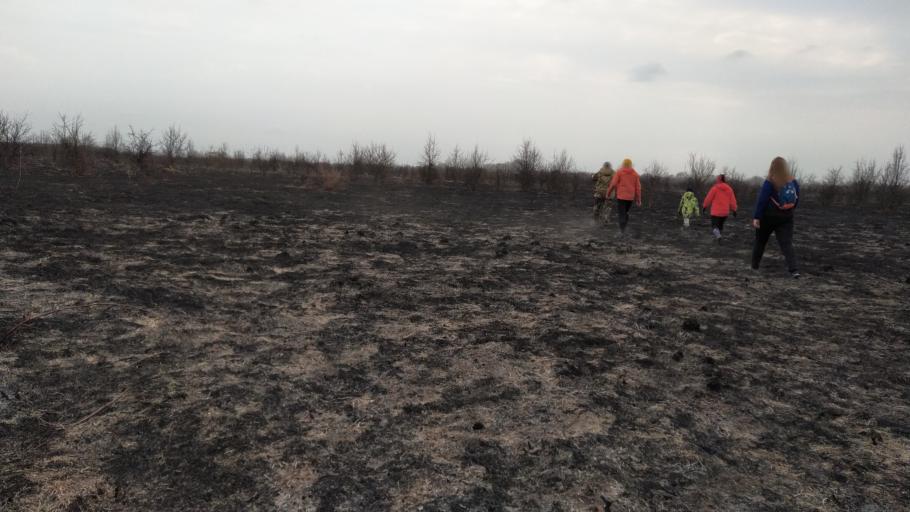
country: RU
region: Rostov
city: Semikarakorsk
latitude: 47.5485
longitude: 40.6810
